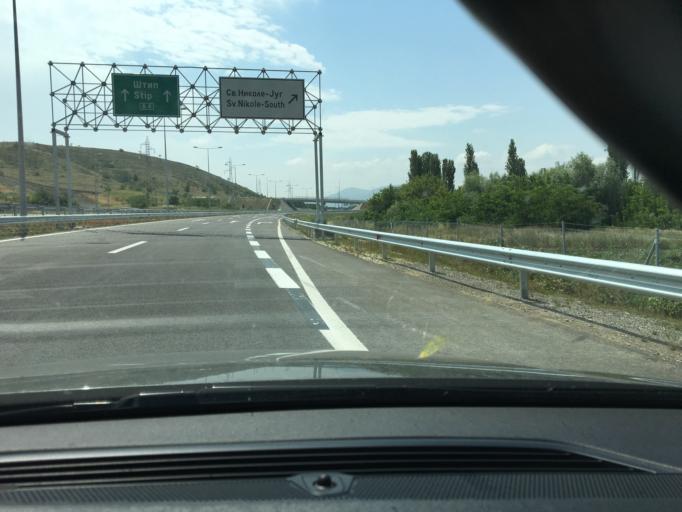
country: MK
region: Sveti Nikole
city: Sveti Nikole
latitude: 41.8585
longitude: 21.9603
